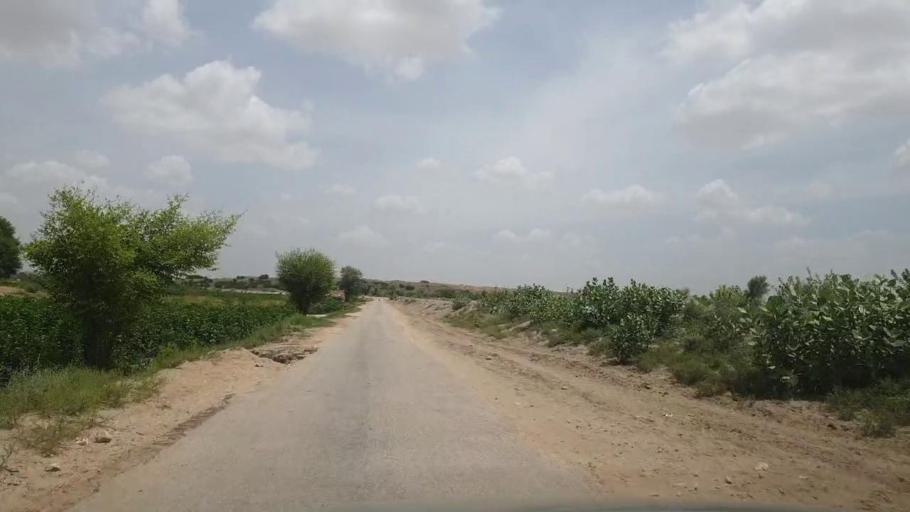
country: PK
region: Sindh
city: Kot Diji
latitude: 27.1999
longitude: 69.0626
